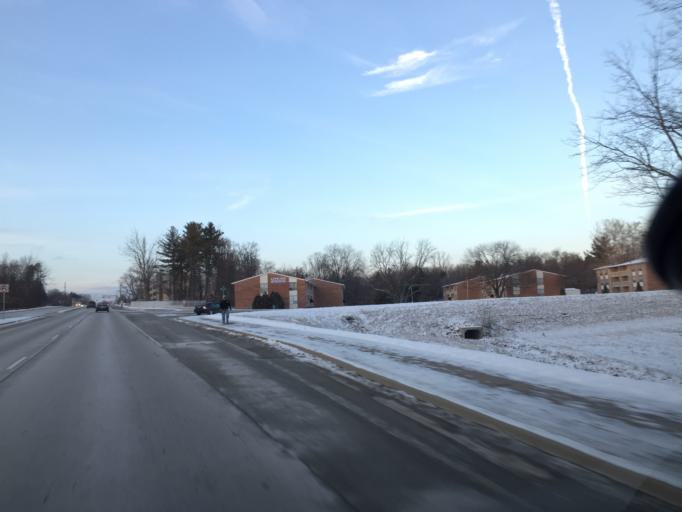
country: US
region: Indiana
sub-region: Monroe County
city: Bloomington
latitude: 39.1670
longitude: -86.4997
